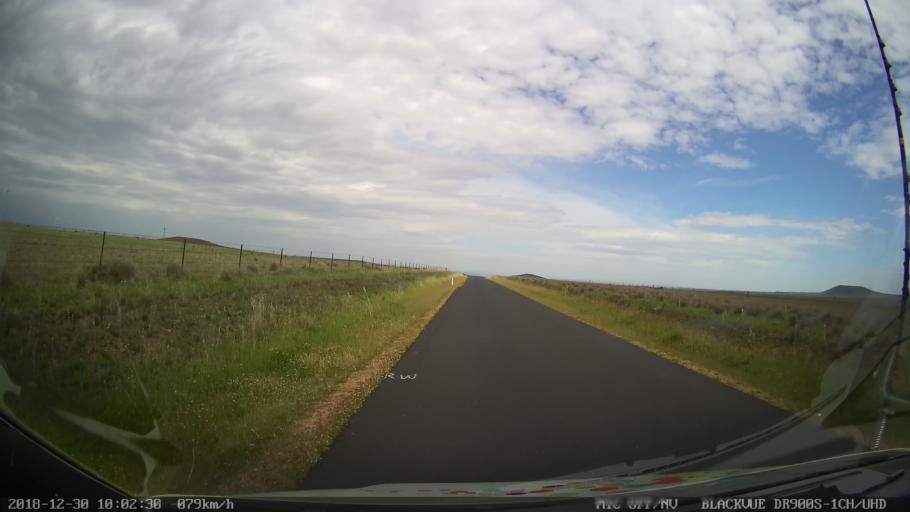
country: AU
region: New South Wales
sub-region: Cooma-Monaro
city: Cooma
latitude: -36.5156
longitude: 149.1712
